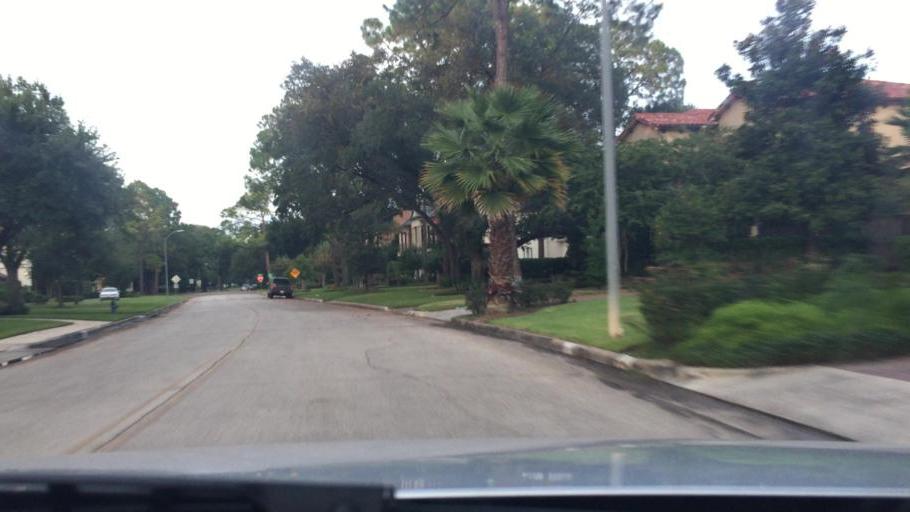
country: US
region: Texas
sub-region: Harris County
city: Hunters Creek Village
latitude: 29.7572
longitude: -95.4751
